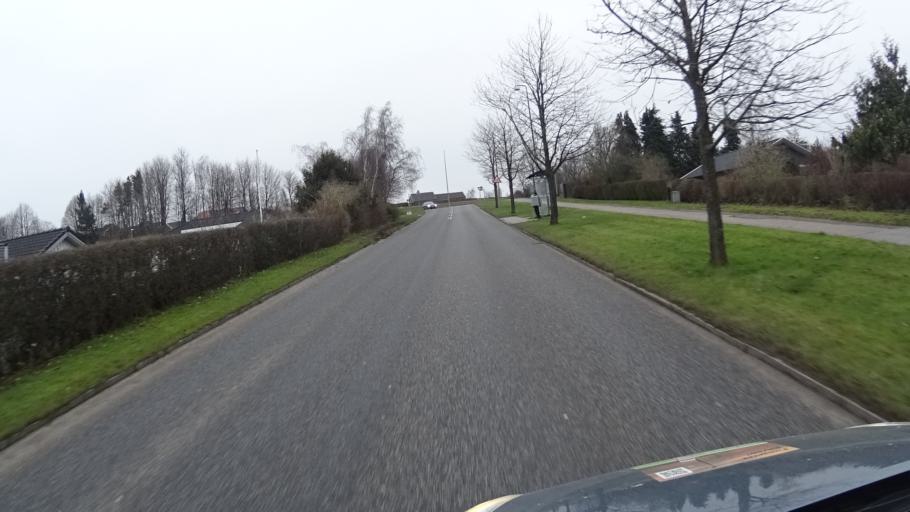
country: DK
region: South Denmark
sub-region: Vejle Kommune
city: Vejle
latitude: 55.7257
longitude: 9.6130
